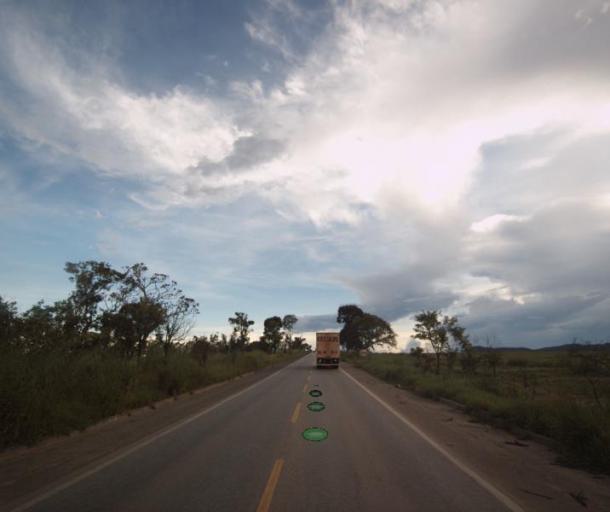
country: BR
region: Goias
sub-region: Uruacu
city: Uruacu
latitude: -14.1350
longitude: -49.1130
